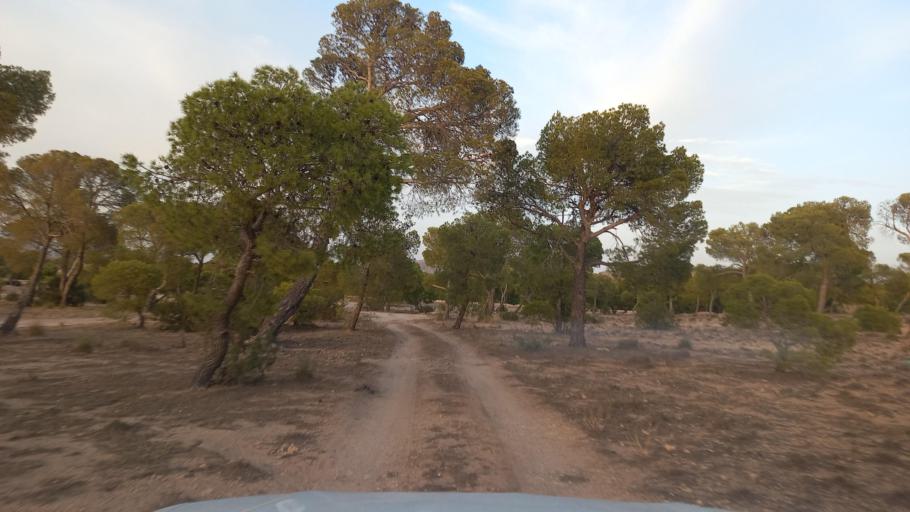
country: TN
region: Al Qasrayn
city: Sbiba
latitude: 35.4256
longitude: 8.9186
